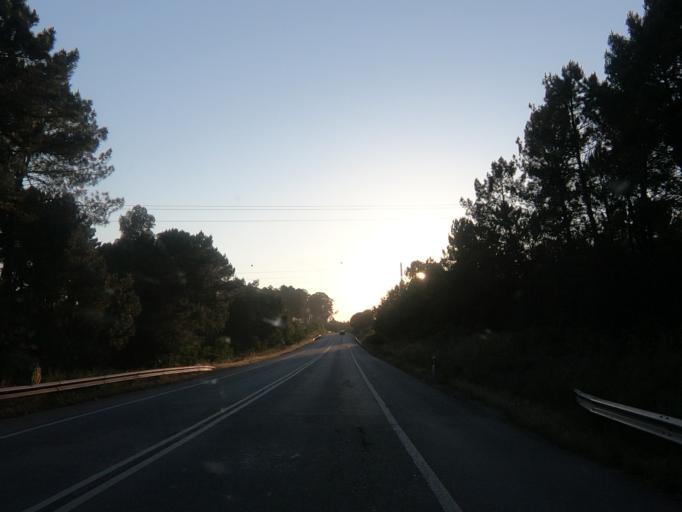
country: PT
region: Viseu
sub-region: Viseu
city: Rio de Loba
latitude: 40.6747
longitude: -7.8645
